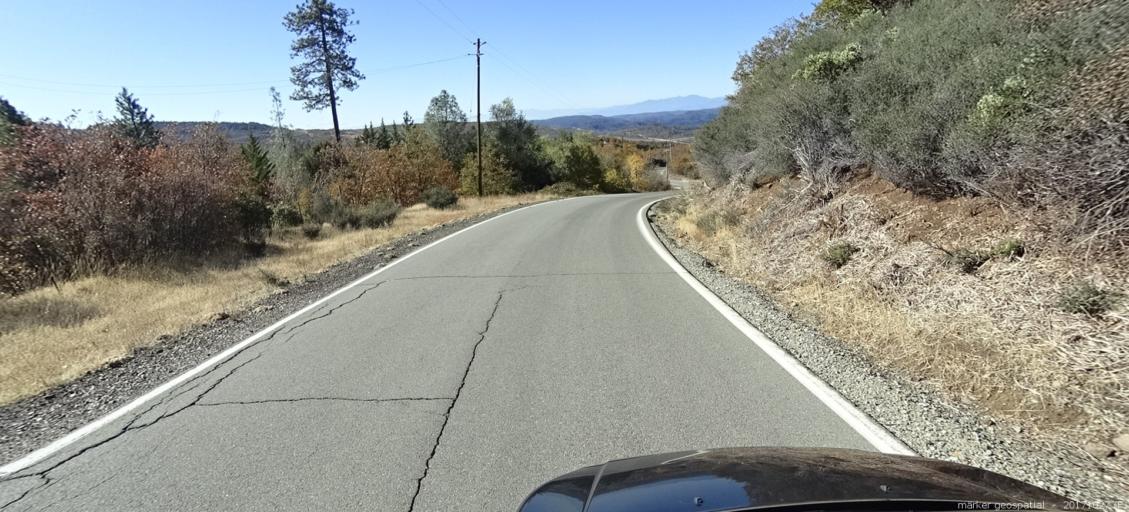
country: US
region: California
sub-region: Shasta County
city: Burney
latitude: 40.7976
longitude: -121.9130
